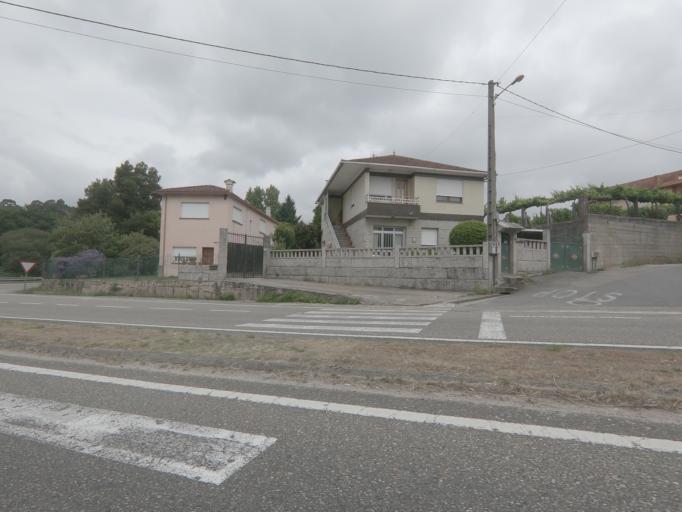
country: PT
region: Viana do Castelo
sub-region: Valenca
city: Valenca
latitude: 42.0379
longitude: -8.6563
